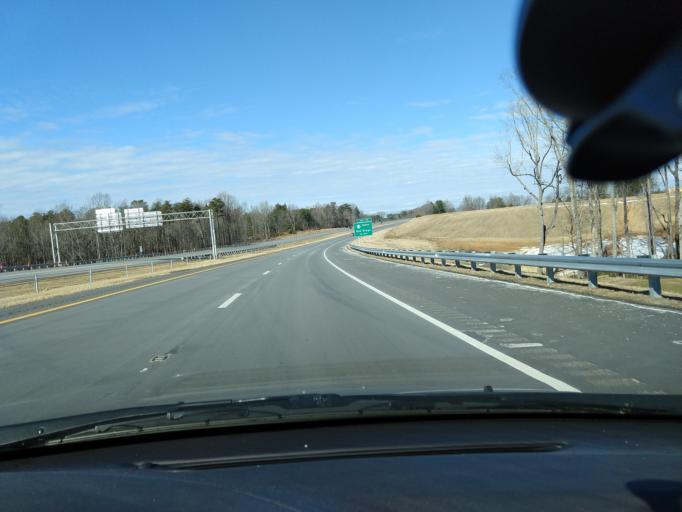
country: US
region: North Carolina
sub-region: Guilford County
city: Oak Ridge
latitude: 36.1268
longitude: -79.9645
